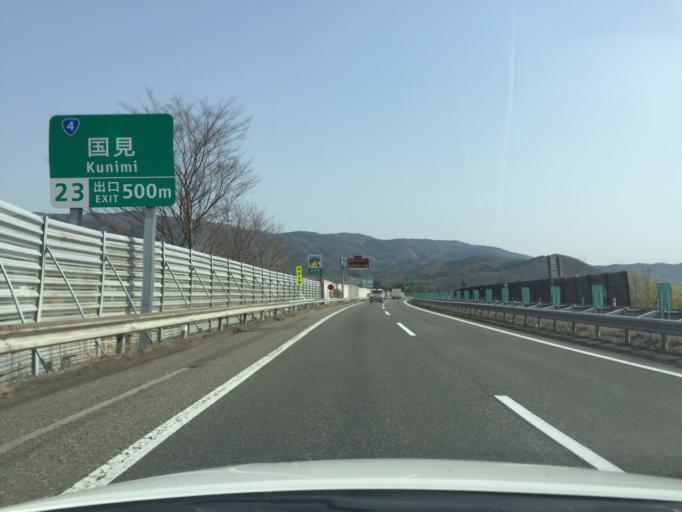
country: JP
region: Fukushima
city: Hobaramachi
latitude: 37.8756
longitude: 140.5250
